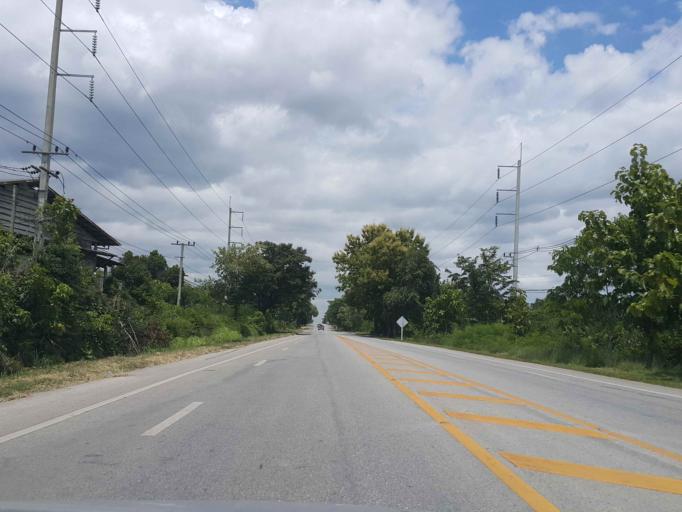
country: TH
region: Lamphun
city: Ban Hong
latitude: 18.3620
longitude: 98.8112
